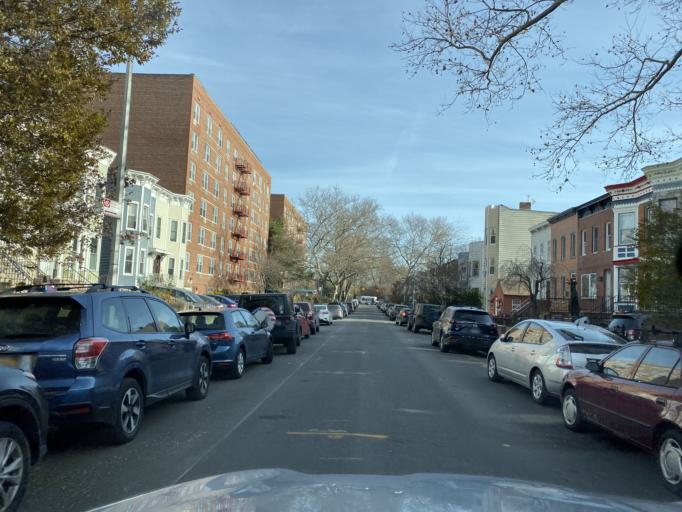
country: US
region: New York
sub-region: Kings County
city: Brooklyn
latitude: 40.6539
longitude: -73.9752
